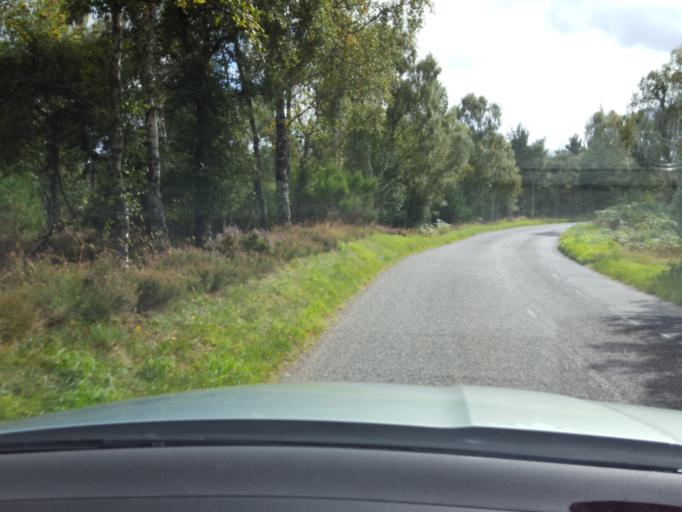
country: GB
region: Scotland
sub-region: Aberdeenshire
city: Ballater
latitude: 57.0797
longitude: -2.9388
